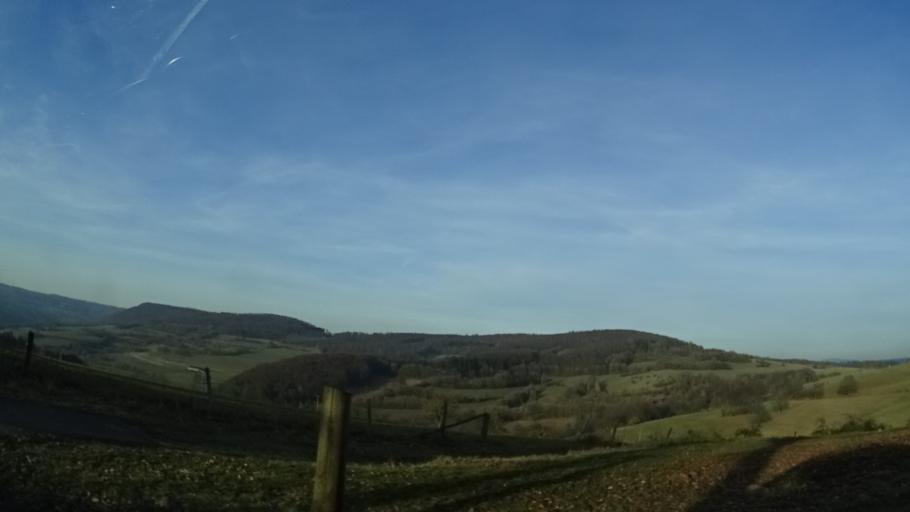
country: DE
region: Bavaria
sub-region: Regierungsbezirk Unterfranken
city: Zeitlofs
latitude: 50.3005
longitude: 9.6863
